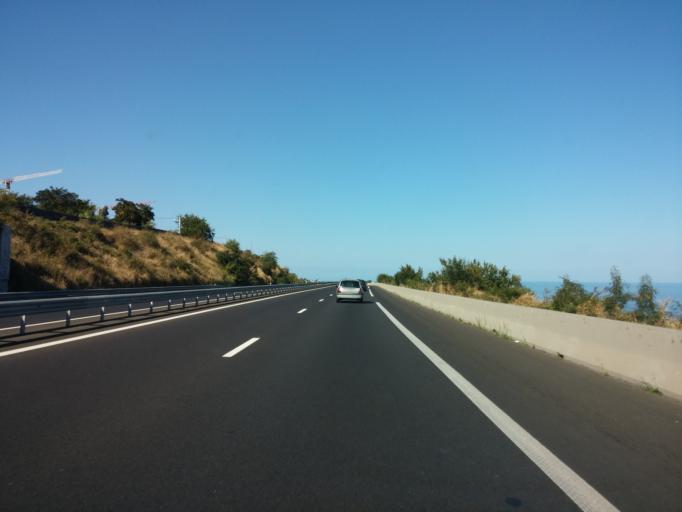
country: RE
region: Reunion
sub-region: Reunion
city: Saint-Leu
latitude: -21.1894
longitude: 55.2968
